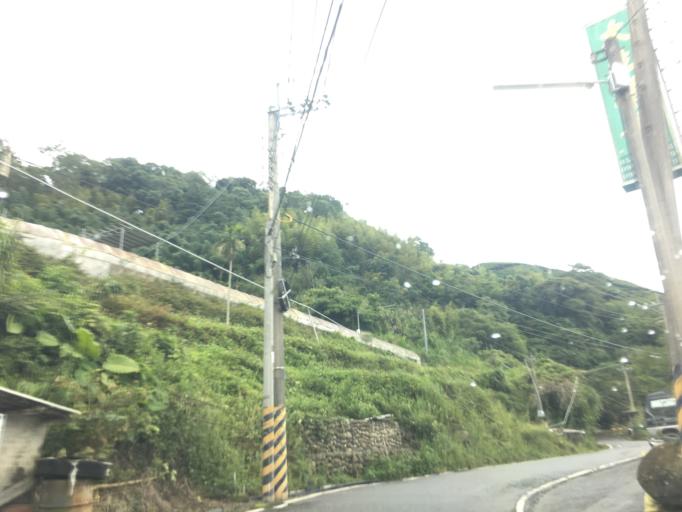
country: TW
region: Taiwan
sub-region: Yunlin
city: Douliu
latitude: 23.5613
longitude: 120.6613
